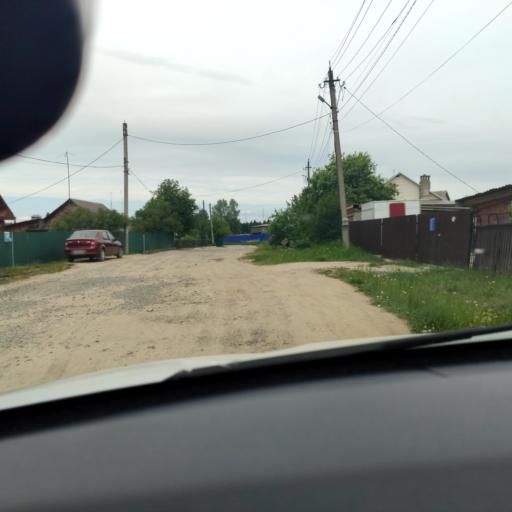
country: RU
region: Perm
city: Polazna
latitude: 58.3012
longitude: 56.3963
